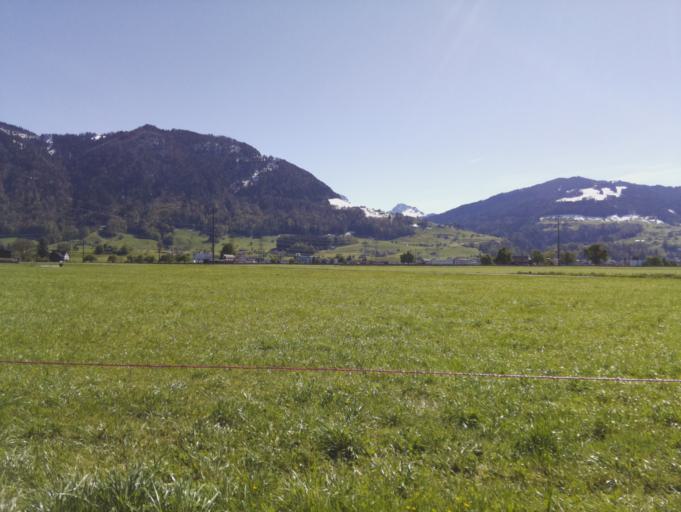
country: CH
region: Schwyz
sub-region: Bezirk March
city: Schubelbach
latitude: 47.1845
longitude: 8.9148
